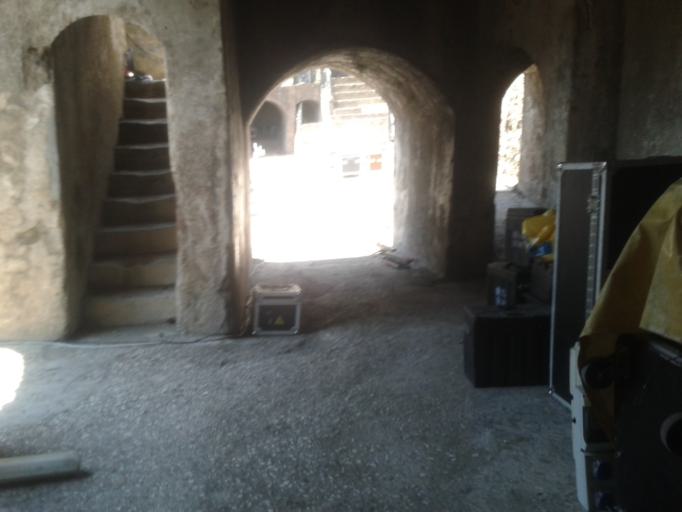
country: IT
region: Campania
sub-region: Provincia di Napoli
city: Pompei
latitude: 40.7489
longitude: 14.4888
